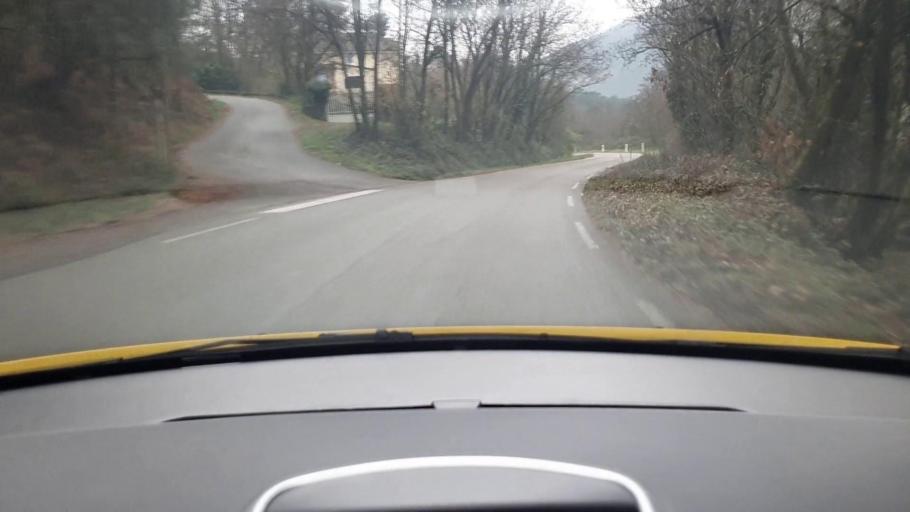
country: FR
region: Languedoc-Roussillon
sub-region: Departement du Gard
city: Besseges
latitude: 44.2629
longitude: 4.0830
